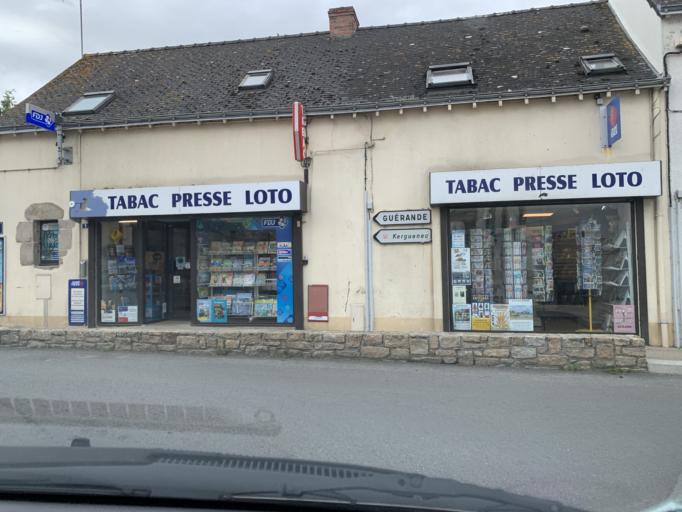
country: FR
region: Pays de la Loire
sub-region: Departement de la Loire-Atlantique
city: Saint-Molf
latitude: 47.3908
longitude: -2.4255
